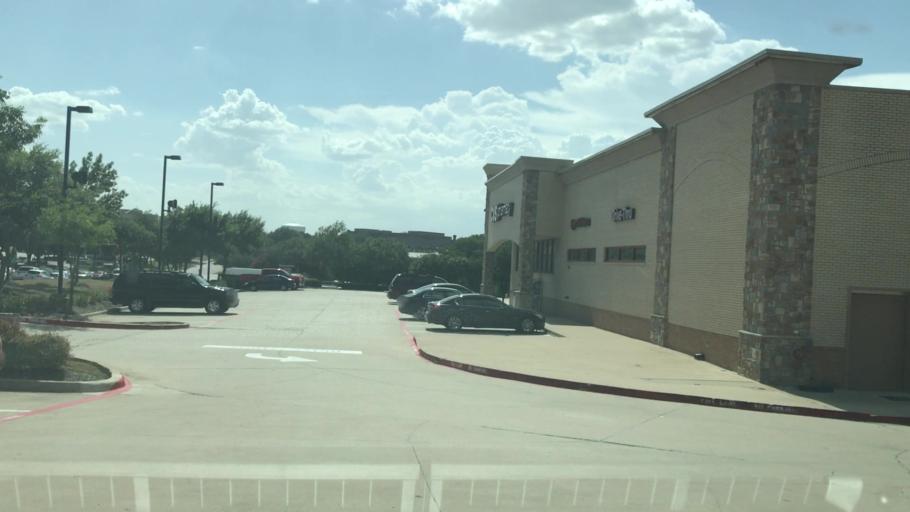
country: US
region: Texas
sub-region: Dallas County
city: Irving
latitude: 32.8854
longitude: -96.9629
